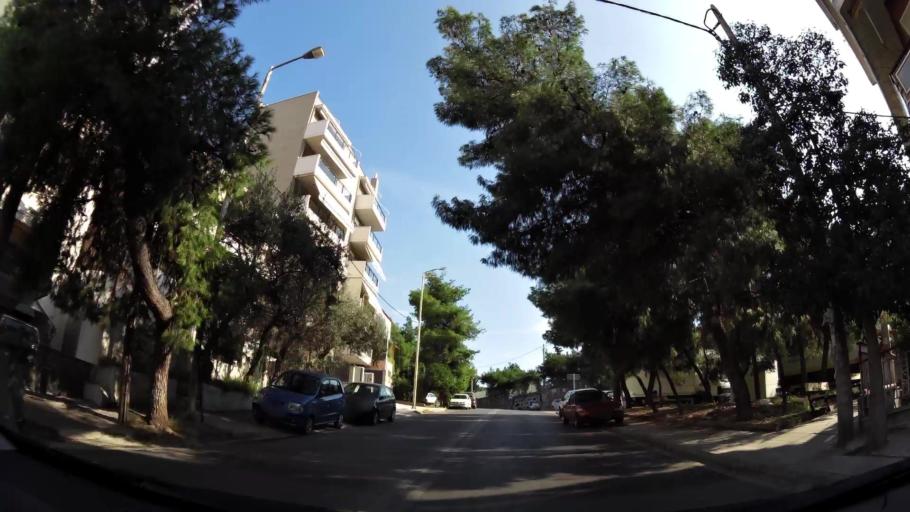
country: GR
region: Attica
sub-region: Nomarchia Athinas
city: Nea Ionia
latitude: 38.0297
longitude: 23.7538
